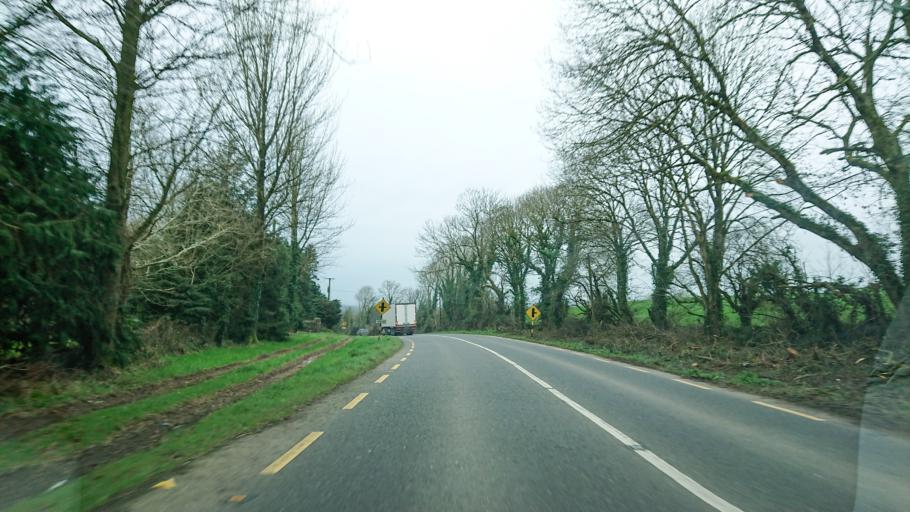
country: IE
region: Munster
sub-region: County Cork
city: Bandon
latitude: 51.7438
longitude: -8.8080
